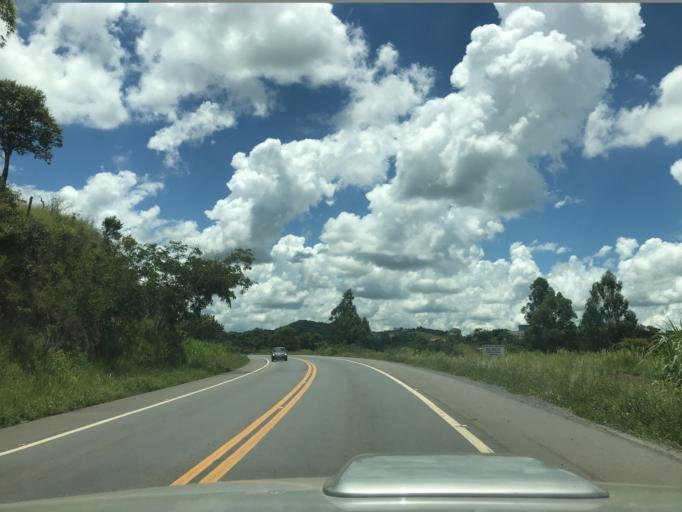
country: BR
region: Minas Gerais
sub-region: Perdoes
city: Perdoes
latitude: -21.0910
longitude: -45.0988
